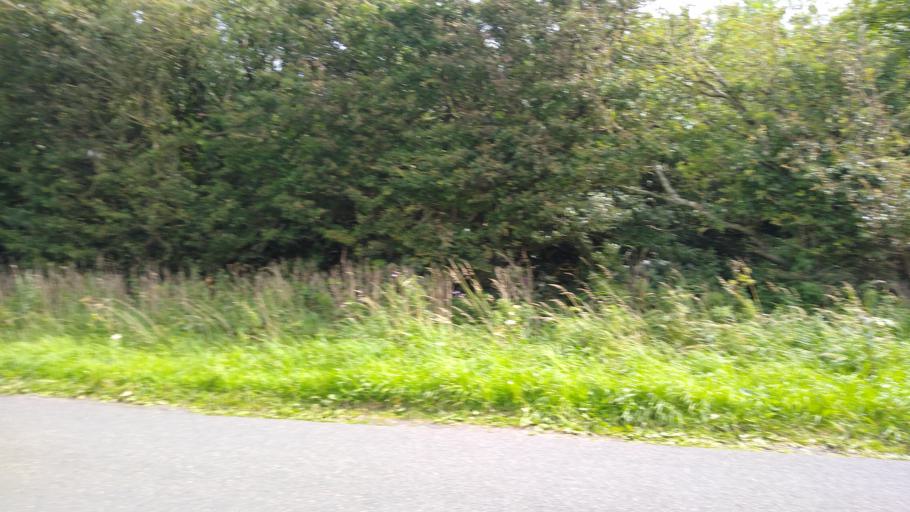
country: GB
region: England
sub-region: Cumbria
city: Dearham
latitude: 54.7894
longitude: -3.4201
